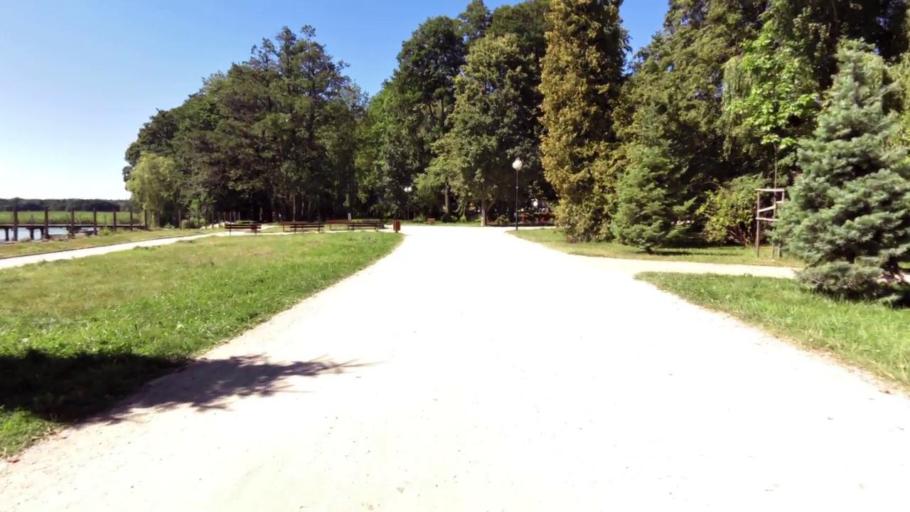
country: PL
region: West Pomeranian Voivodeship
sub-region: Powiat szczecinecki
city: Szczecinek
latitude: 53.7083
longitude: 16.6885
